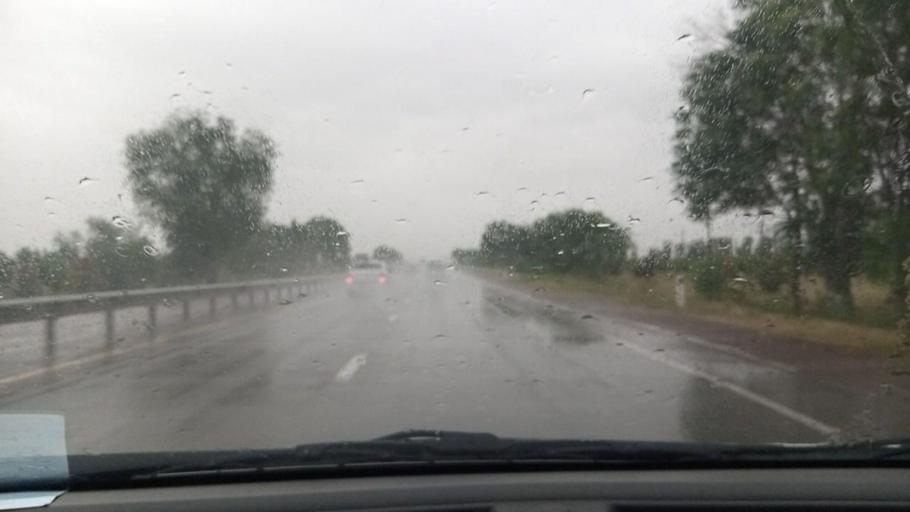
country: UZ
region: Toshkent
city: Ohangaron
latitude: 40.9358
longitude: 69.5880
